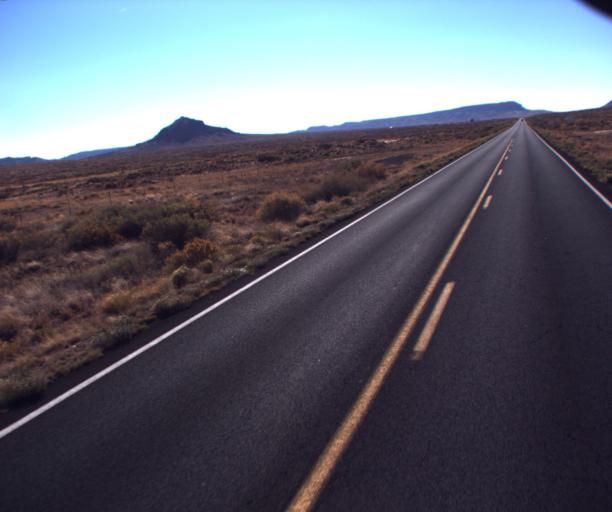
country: US
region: Arizona
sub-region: Navajo County
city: Dilkon
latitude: 35.4920
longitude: -110.4315
